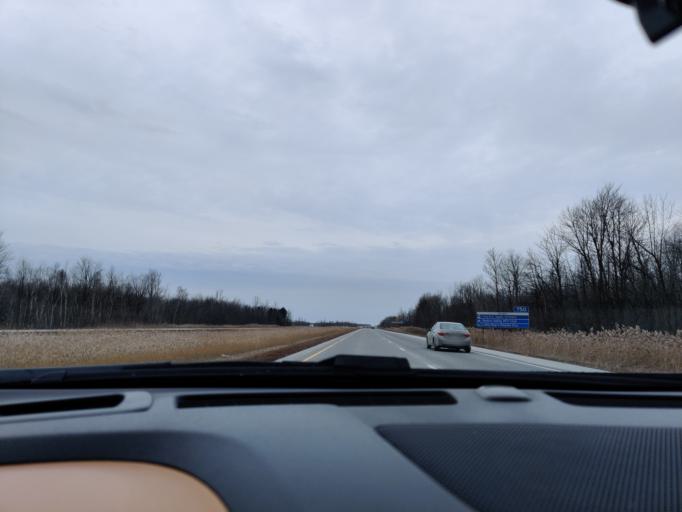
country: US
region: New York
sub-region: St. Lawrence County
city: Norfolk
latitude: 44.9265
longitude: -75.1756
